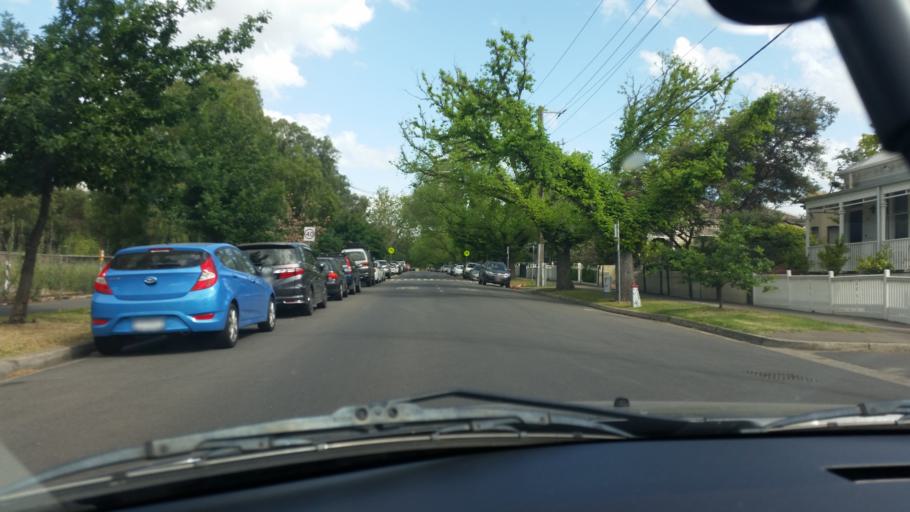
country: AU
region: Victoria
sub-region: Moonee Valley
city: Flemington
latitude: -37.7905
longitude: 144.9295
